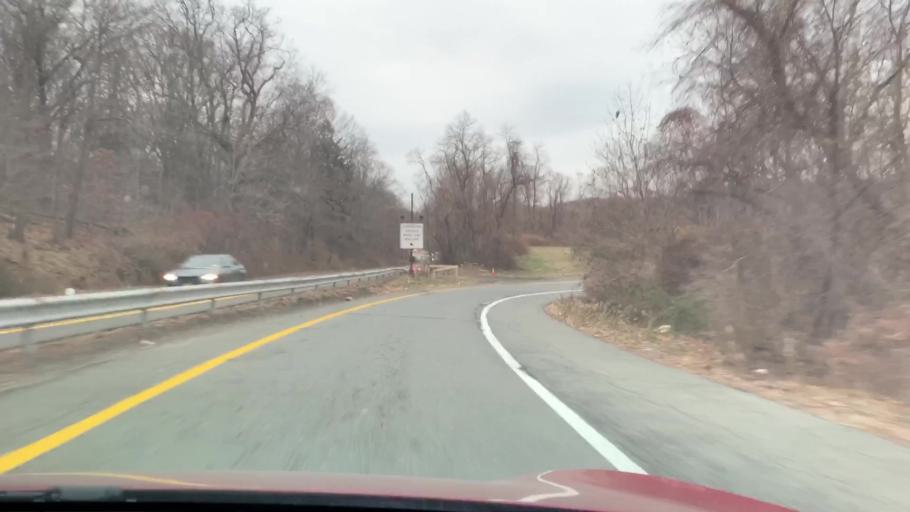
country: US
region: New York
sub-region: Westchester County
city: Purchase
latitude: 41.0126
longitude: -73.7161
